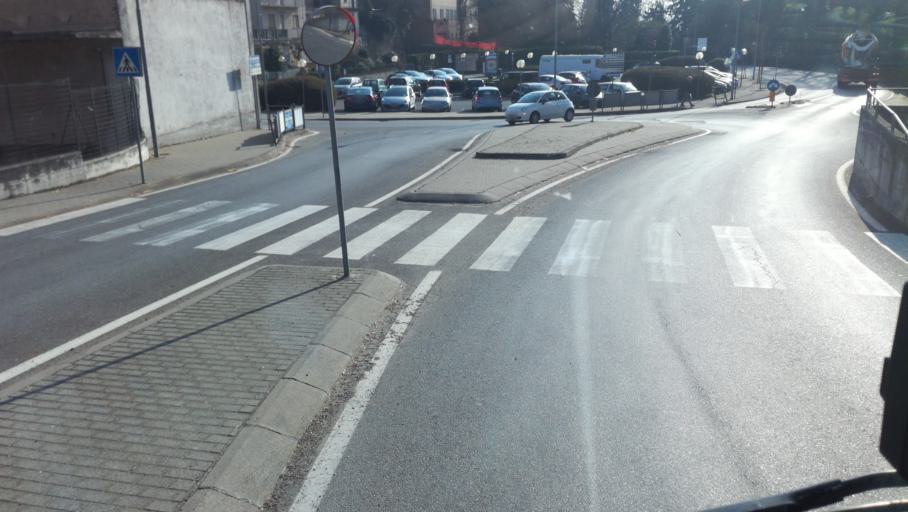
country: IT
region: Piedmont
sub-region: Provincia di Novara
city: Oleggio
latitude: 45.5954
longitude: 8.6345
